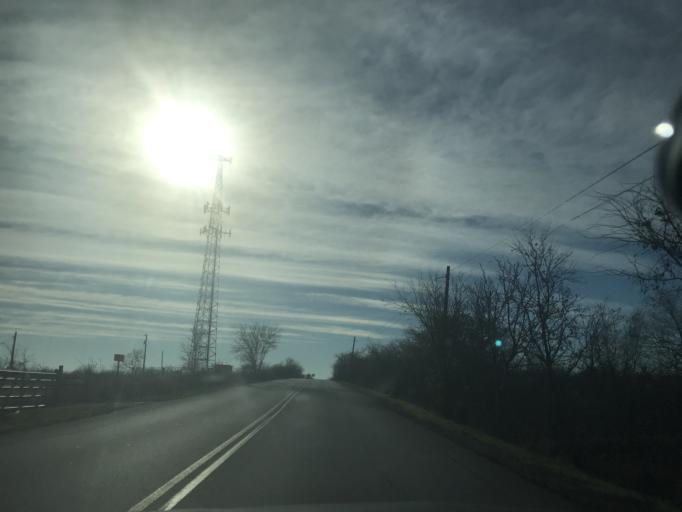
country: US
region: Texas
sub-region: Travis County
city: Manor
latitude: 30.3322
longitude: -97.5488
